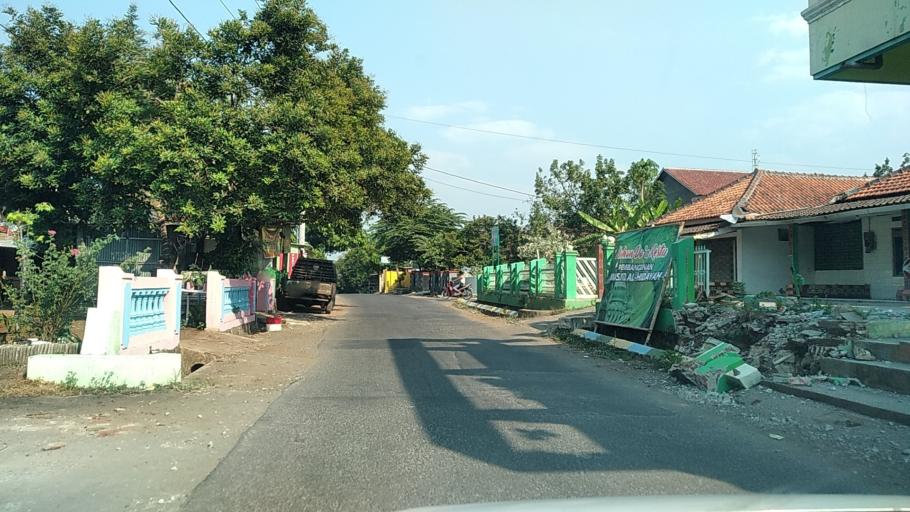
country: ID
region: Central Java
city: Semarang
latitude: -7.0522
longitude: 110.3282
